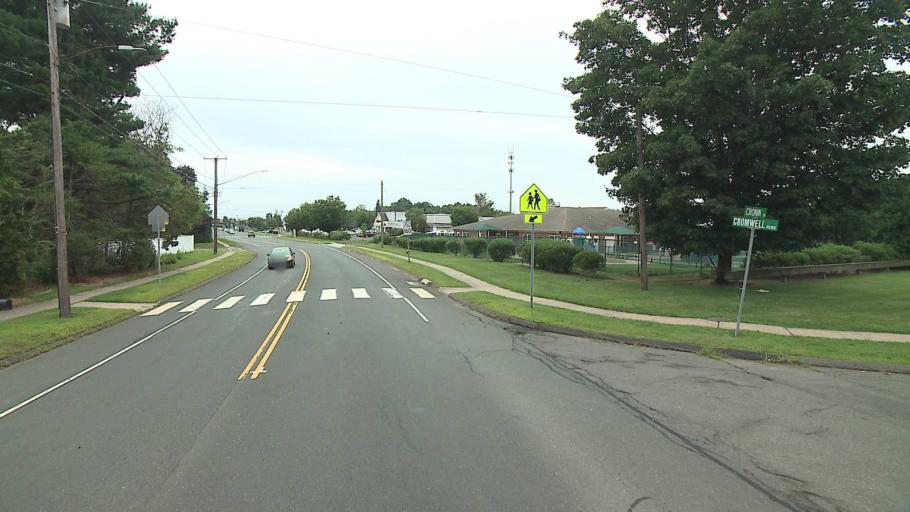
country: US
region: Connecticut
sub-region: Hartford County
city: Newington
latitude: 41.6626
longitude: -72.6788
